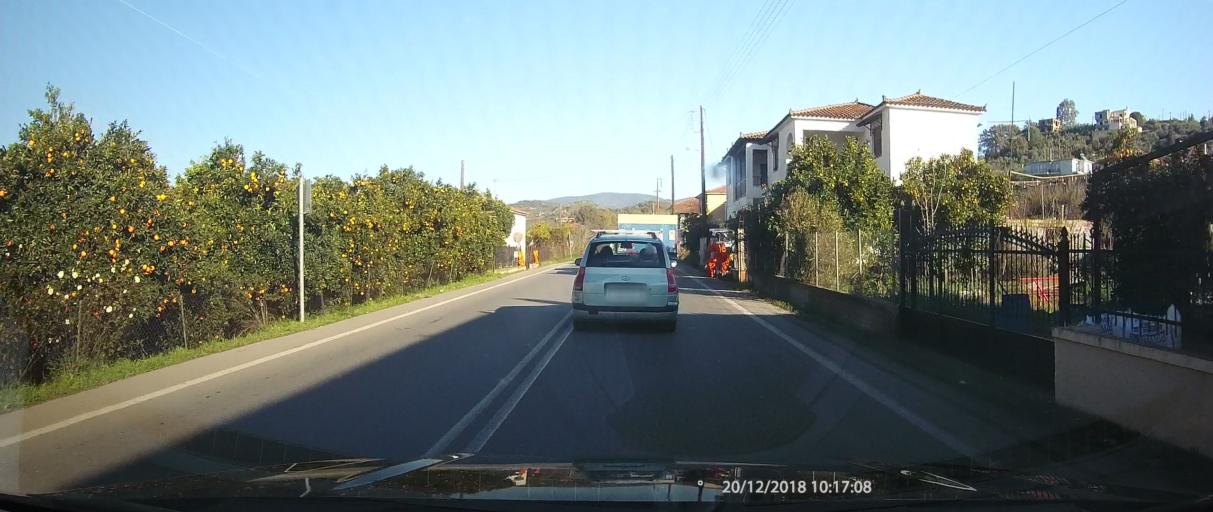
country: GR
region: Peloponnese
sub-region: Nomos Lakonias
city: Sparti
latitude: 37.1035
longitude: 22.4340
